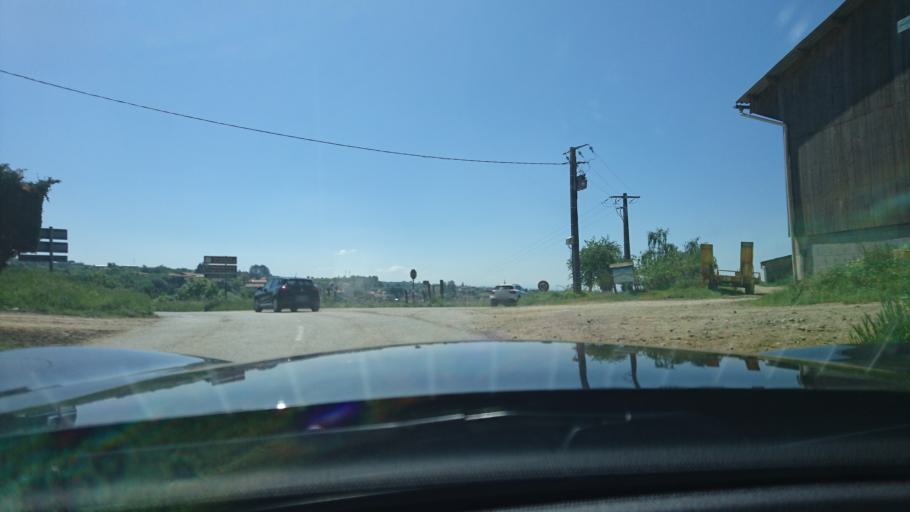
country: FR
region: Rhone-Alpes
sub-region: Departement de la Loire
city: Bussieres
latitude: 45.8432
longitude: 4.2646
